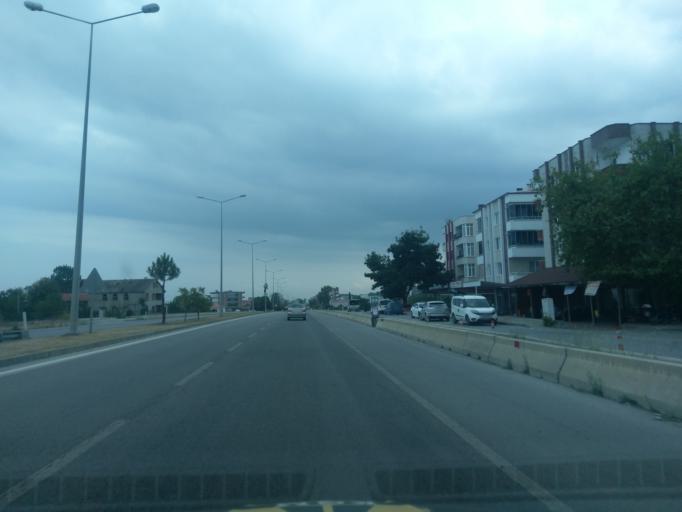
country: TR
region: Samsun
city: Taflan
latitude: 41.4066
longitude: 36.1805
